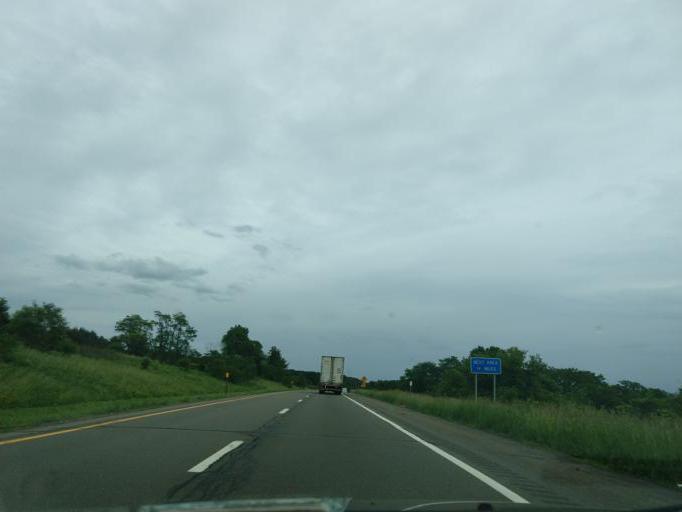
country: US
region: New York
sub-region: Chenango County
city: Lakeview
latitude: 42.3905
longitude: -76.0007
